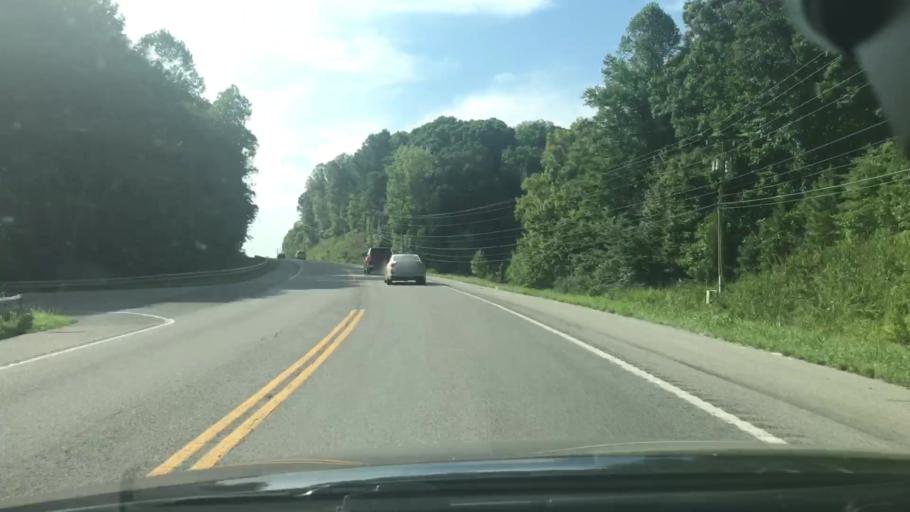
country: US
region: Tennessee
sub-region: Williamson County
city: Franklin
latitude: 35.9676
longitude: -86.9701
